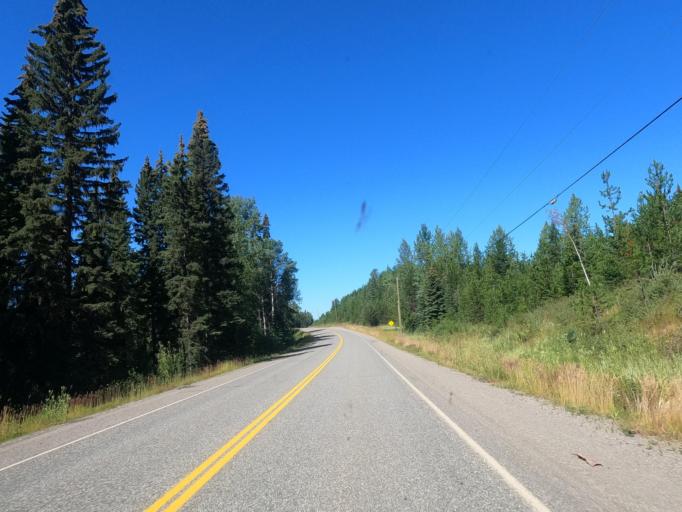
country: CA
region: British Columbia
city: Quesnel
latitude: 53.0298
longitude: -122.1026
